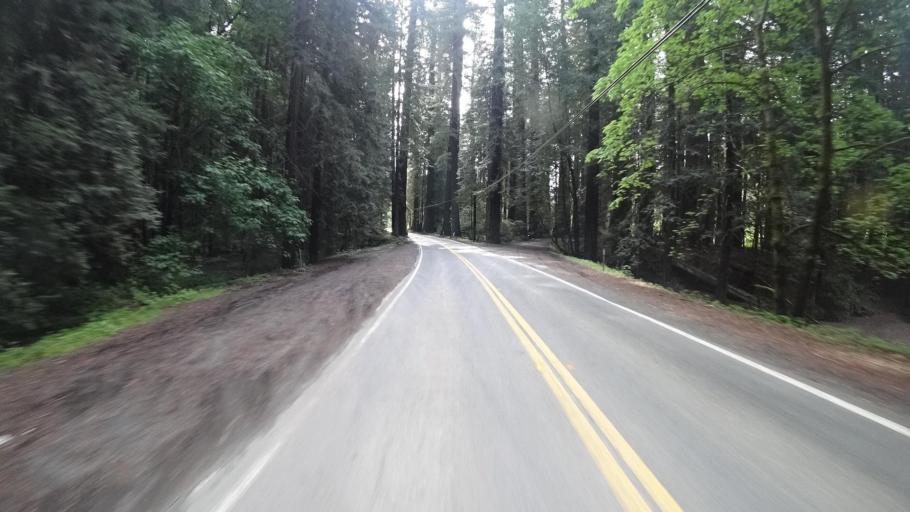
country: US
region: California
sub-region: Humboldt County
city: Redway
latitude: 40.2227
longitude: -123.8011
